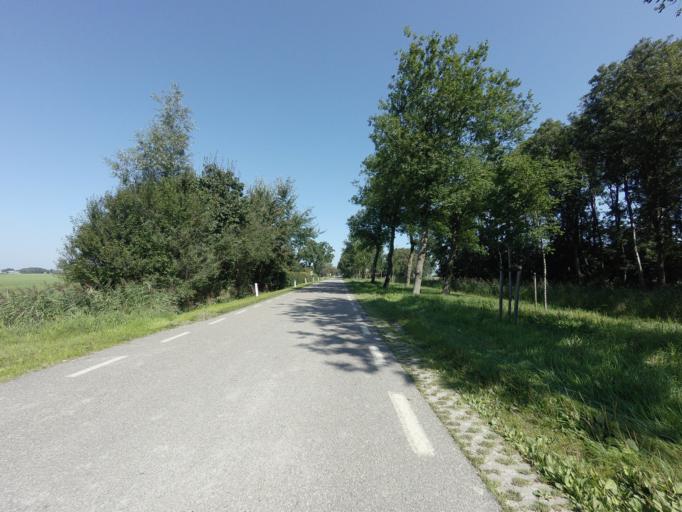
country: NL
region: Friesland
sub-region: Gemeente Dongeradeel
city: Ternaard
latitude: 53.3740
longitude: 5.9988
